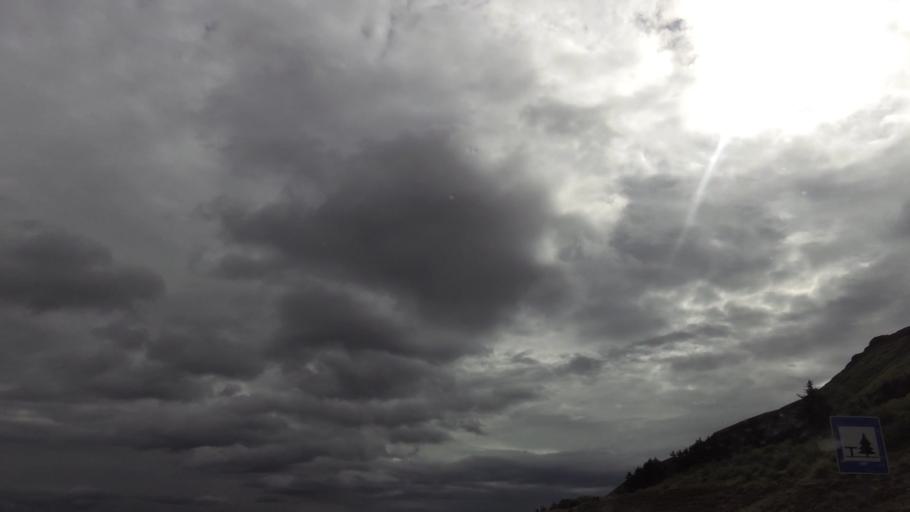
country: IS
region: West
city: Stykkisholmur
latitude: 65.5131
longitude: -22.1109
